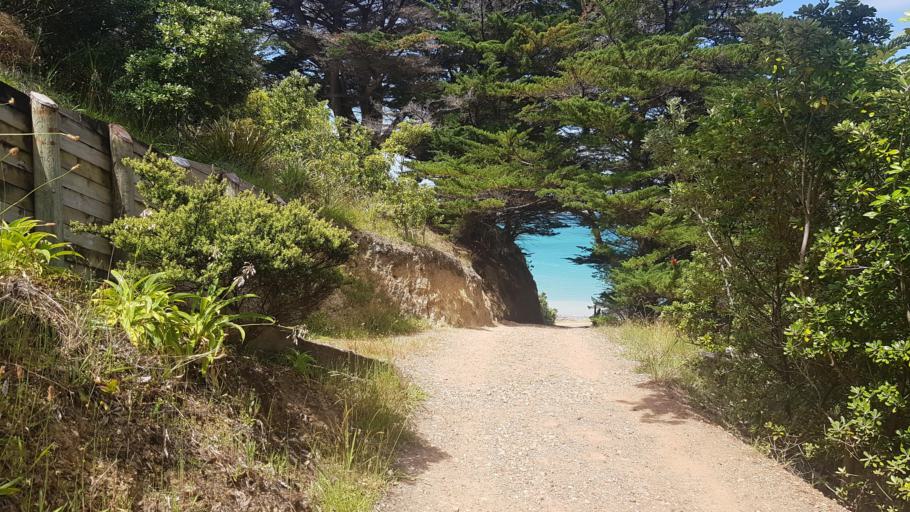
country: NZ
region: Auckland
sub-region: Auckland
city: Pakuranga
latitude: -36.8443
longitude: 175.1480
